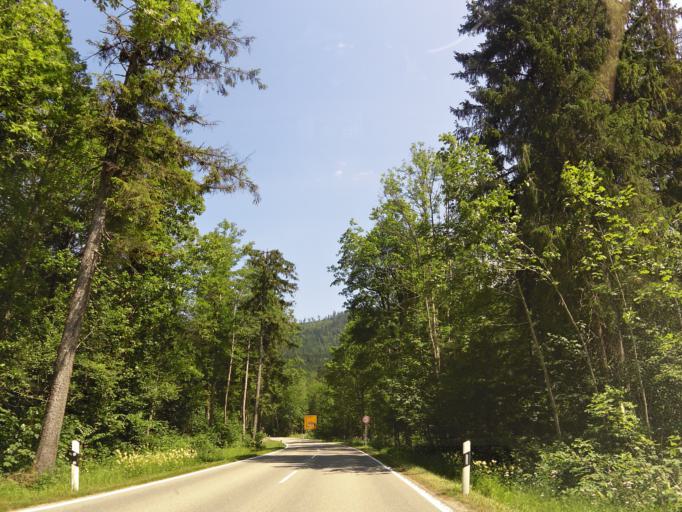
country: DE
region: Bavaria
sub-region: Upper Bavaria
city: Reit im Winkl
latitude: 47.6577
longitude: 12.5346
